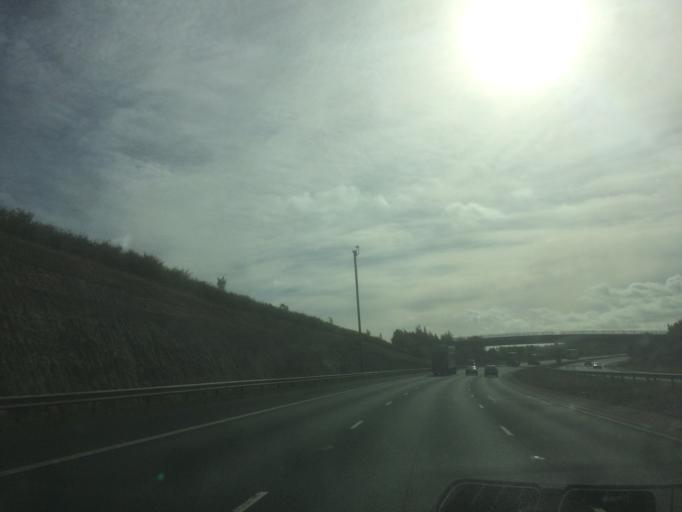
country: GB
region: England
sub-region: City and Borough of Leeds
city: Aberford
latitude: 53.7973
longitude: -1.3248
